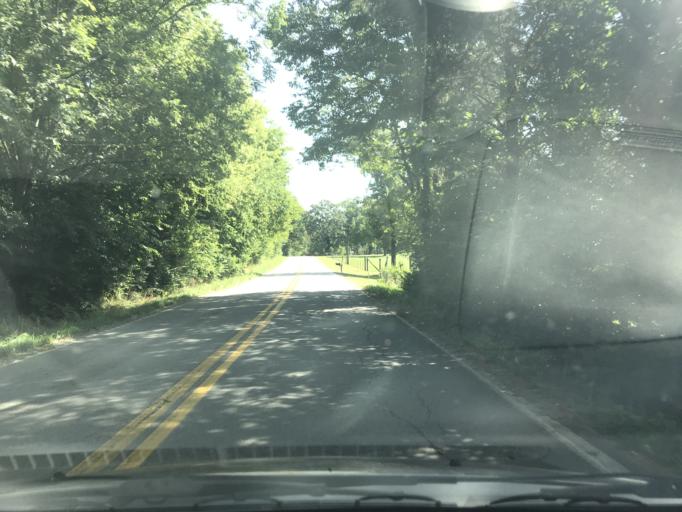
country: US
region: Tennessee
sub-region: Hamilton County
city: Lakesite
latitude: 35.2694
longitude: -85.0583
